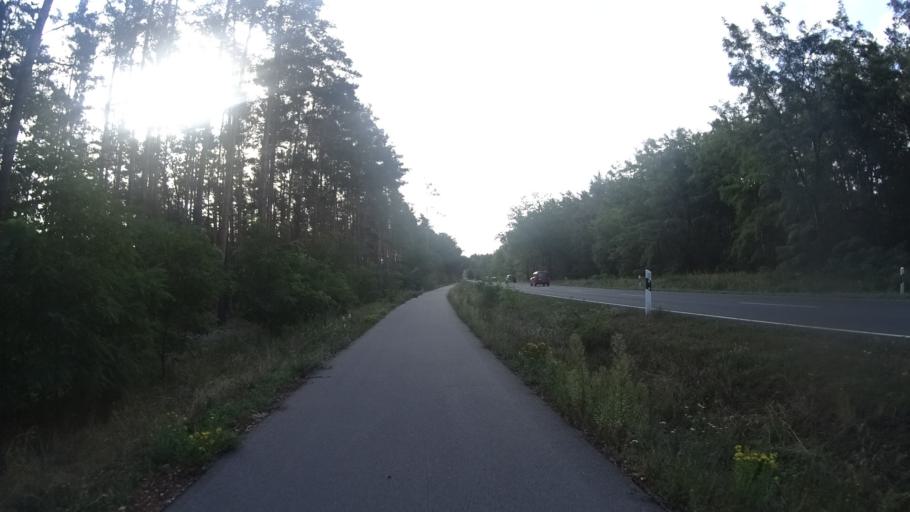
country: DE
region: Brandenburg
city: Premnitz
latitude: 52.5186
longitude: 12.3986
